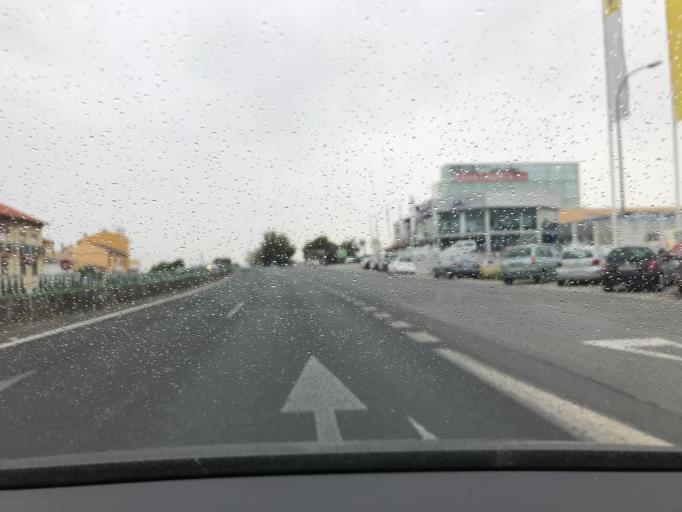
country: ES
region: Andalusia
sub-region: Provincia de Granada
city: Atarfe
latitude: 37.1927
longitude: -3.7209
